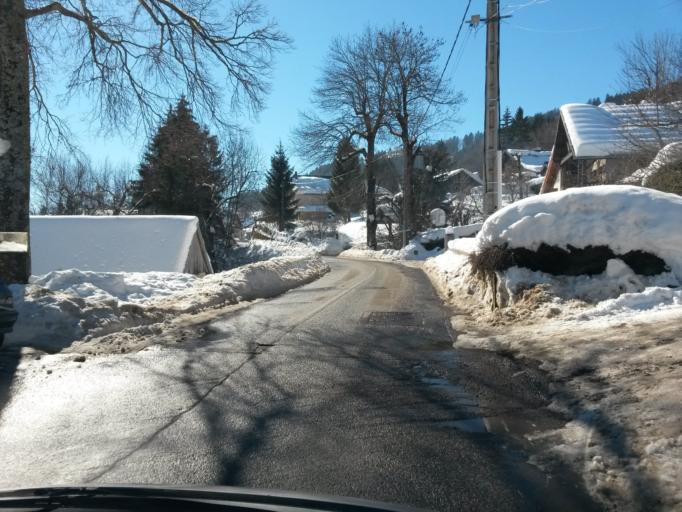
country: FR
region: Rhone-Alpes
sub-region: Departement de l'Isere
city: Saint-Hilaire
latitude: 45.3180
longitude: 5.8888
